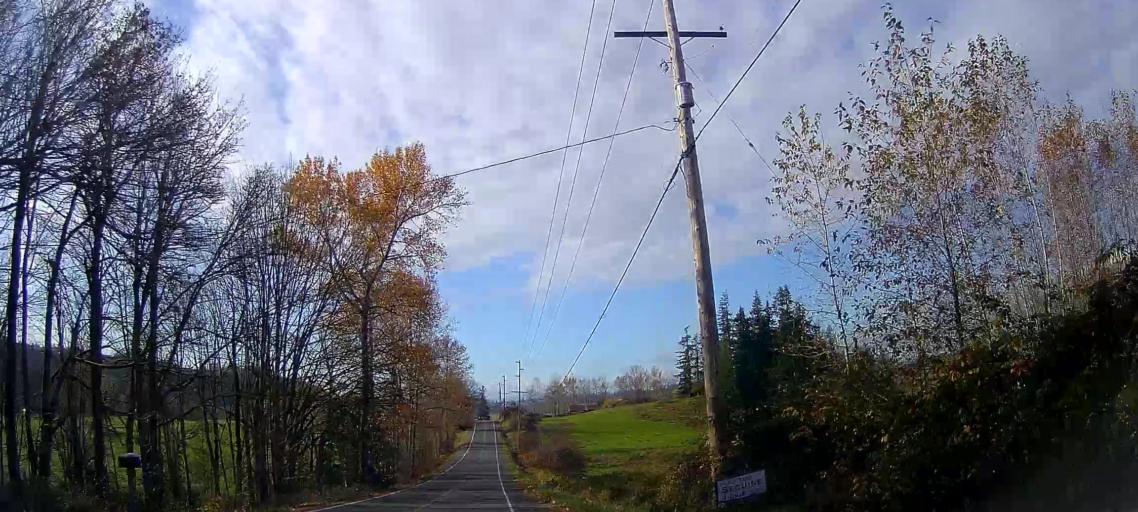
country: US
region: Washington
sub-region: Skagit County
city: Big Lake
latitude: 48.4353
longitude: -122.2584
